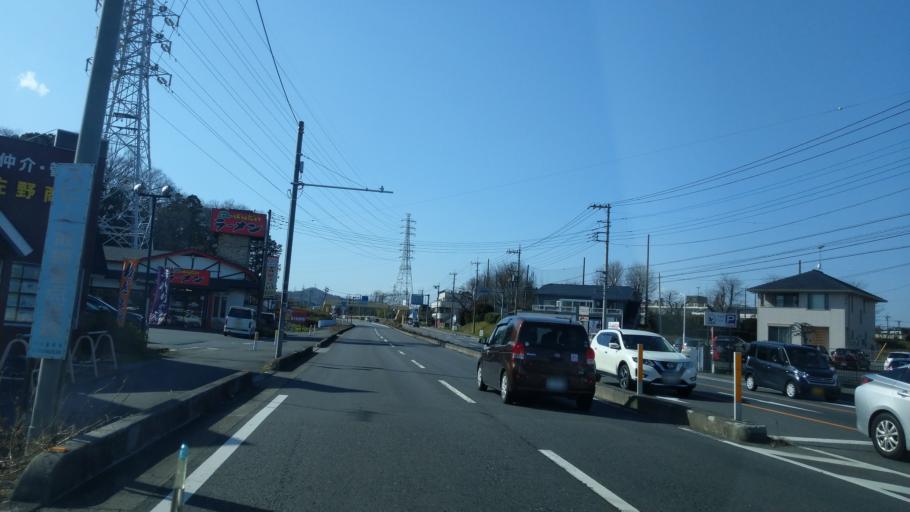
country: JP
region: Saitama
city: Ogawa
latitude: 36.0370
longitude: 139.3254
